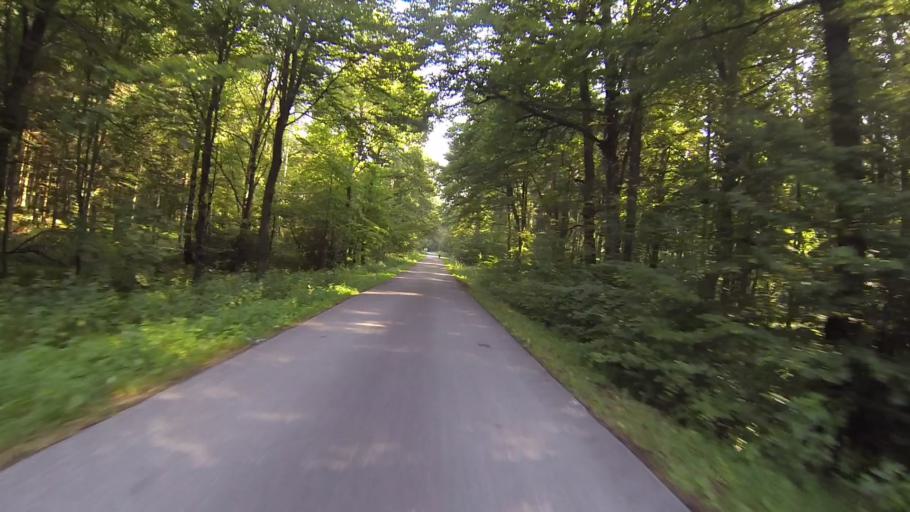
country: DE
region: Baden-Wuerttemberg
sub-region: Regierungsbezirk Stuttgart
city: Konigsbronn
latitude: 48.7150
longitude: 10.1107
